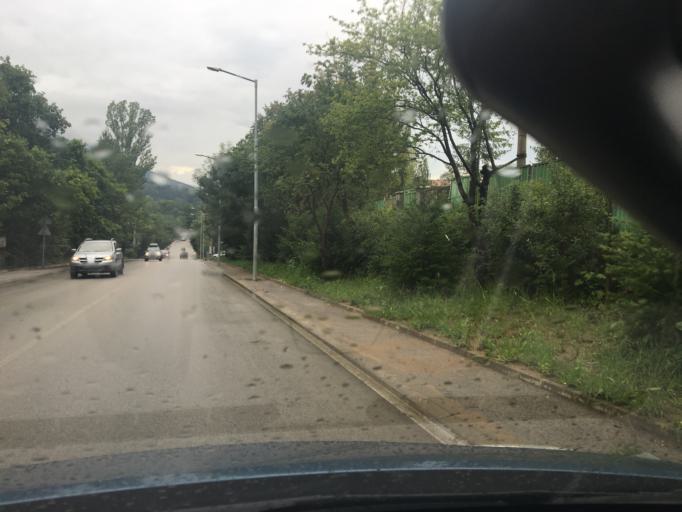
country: BG
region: Sofia-Capital
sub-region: Stolichna Obshtina
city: Sofia
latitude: 42.6425
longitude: 23.2890
